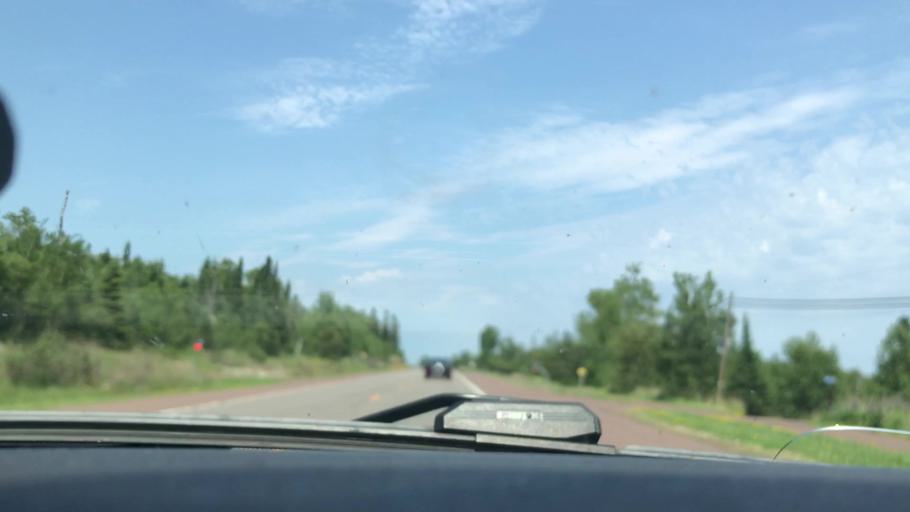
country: US
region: Minnesota
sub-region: Cook County
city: Grand Marais
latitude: 47.5916
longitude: -90.8021
